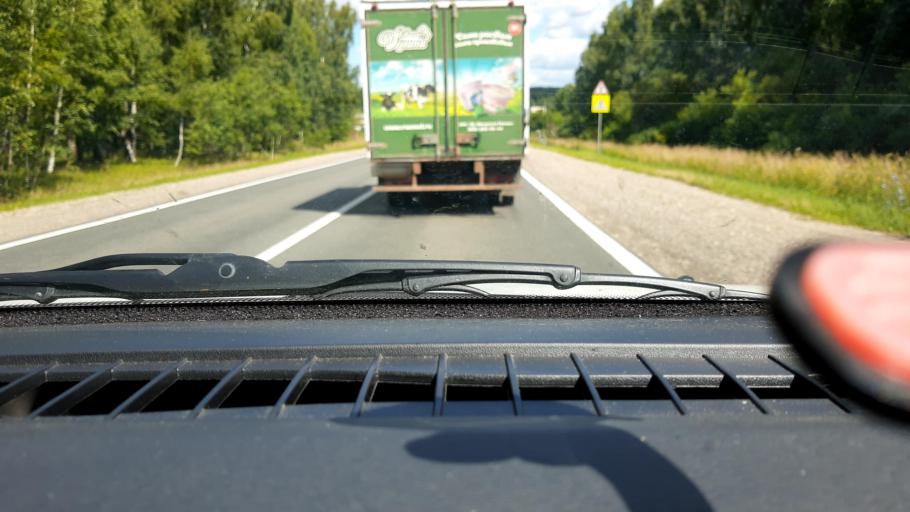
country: RU
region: Nizjnij Novgorod
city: Surovatikha
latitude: 55.7685
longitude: 43.9983
